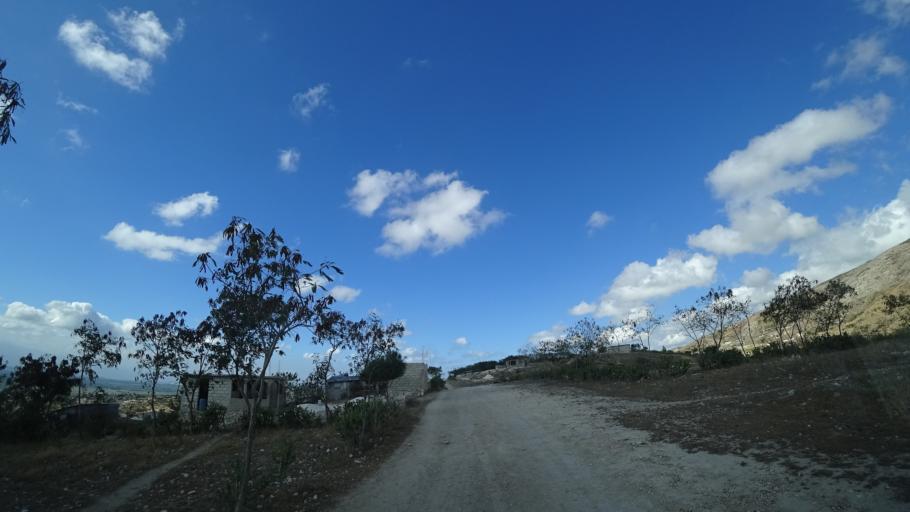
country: HT
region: Ouest
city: Croix des Bouquets
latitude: 18.6724
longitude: -72.2686
